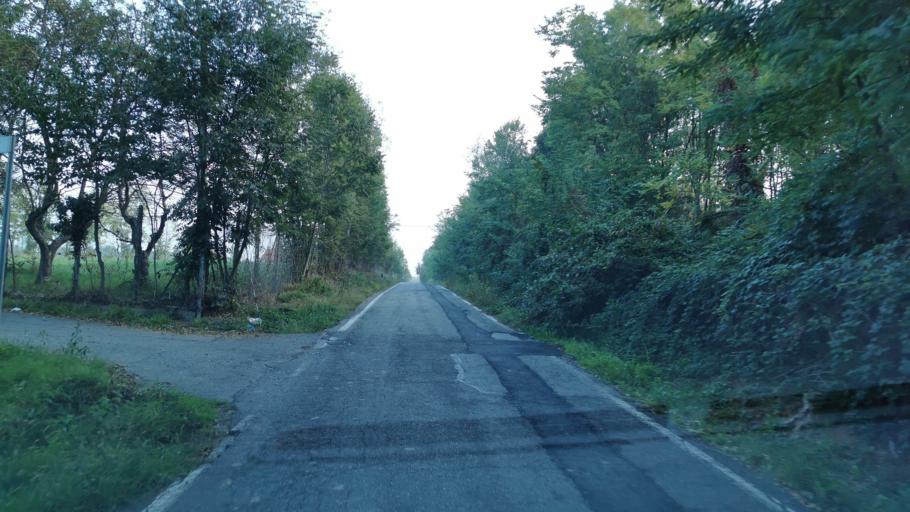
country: IT
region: Piedmont
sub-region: Provincia di Torino
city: San Carlo Canavese
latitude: 45.2511
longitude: 7.6217
